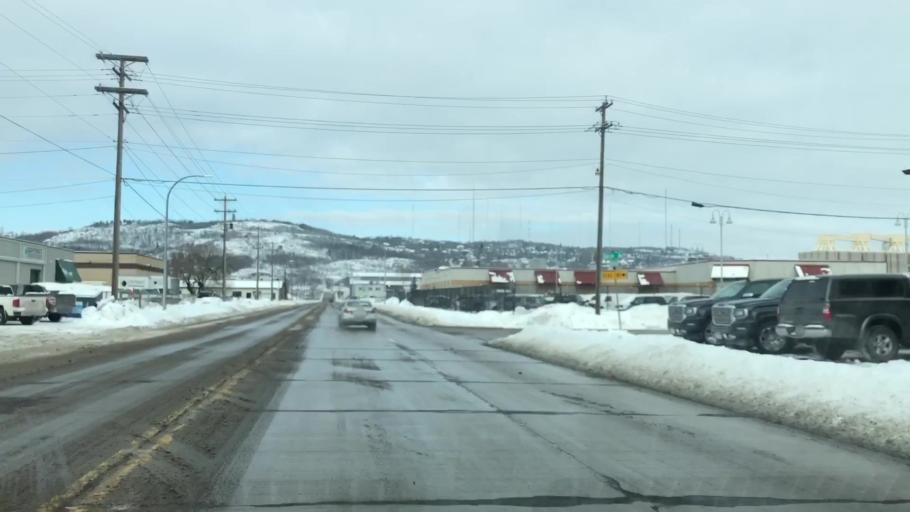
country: US
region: Minnesota
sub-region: Saint Louis County
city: Duluth
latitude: 46.7612
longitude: -92.1103
